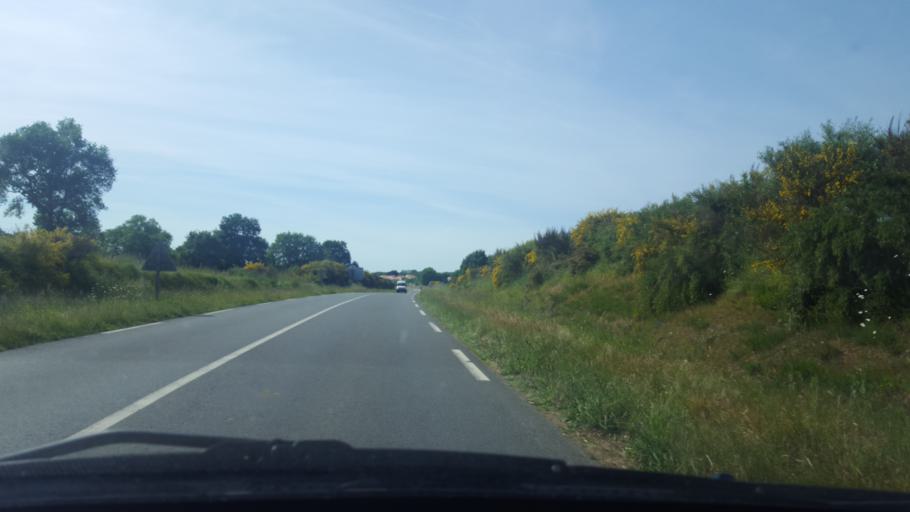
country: FR
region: Pays de la Loire
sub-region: Departement de la Loire-Atlantique
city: Saint-Philbert-de-Grand-Lieu
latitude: 47.0283
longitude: -1.6450
